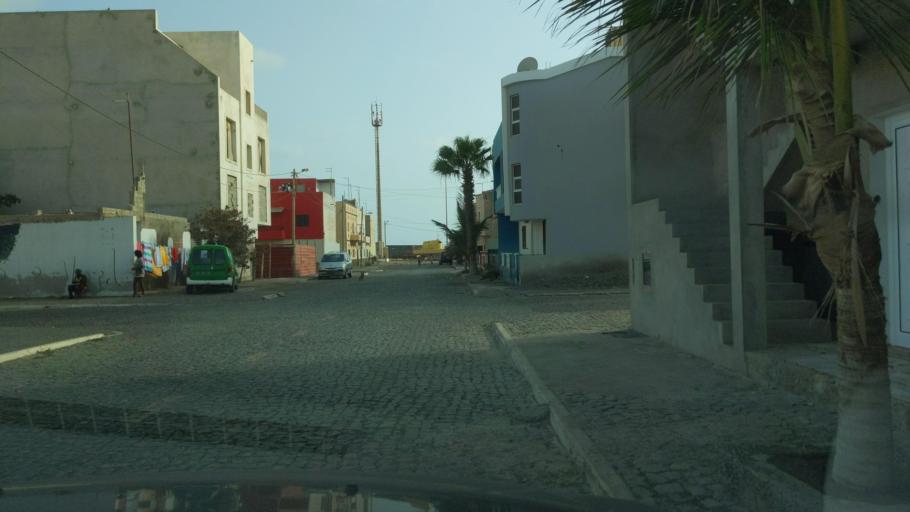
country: CV
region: Sal
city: Espargos
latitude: 16.7593
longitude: -22.9820
